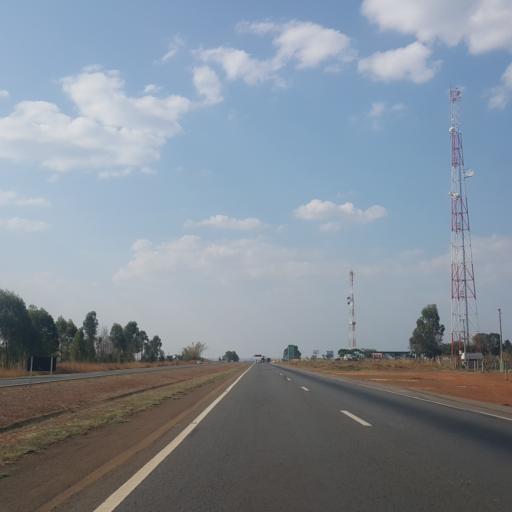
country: BR
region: Goias
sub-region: Abadiania
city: Abadiania
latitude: -16.2202
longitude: -48.7493
